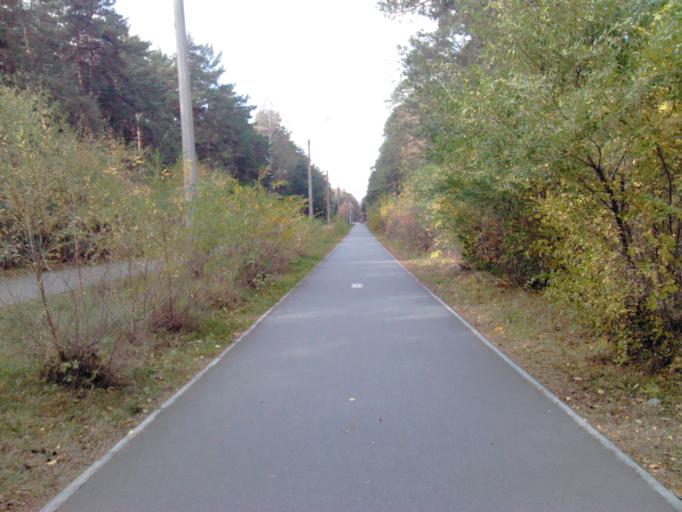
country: RU
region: Chelyabinsk
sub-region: Gorod Chelyabinsk
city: Chelyabinsk
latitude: 55.1634
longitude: 61.3627
